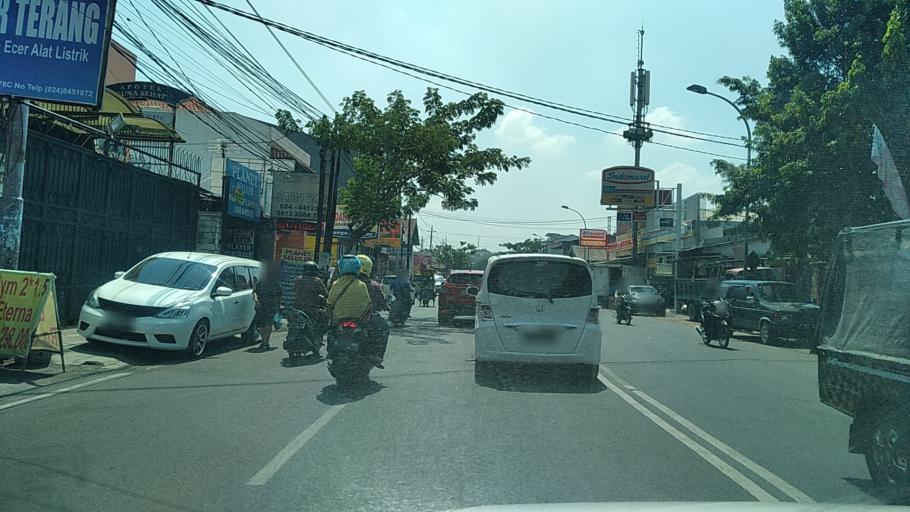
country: ID
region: Central Java
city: Semarang
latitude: -7.0101
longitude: 110.4394
